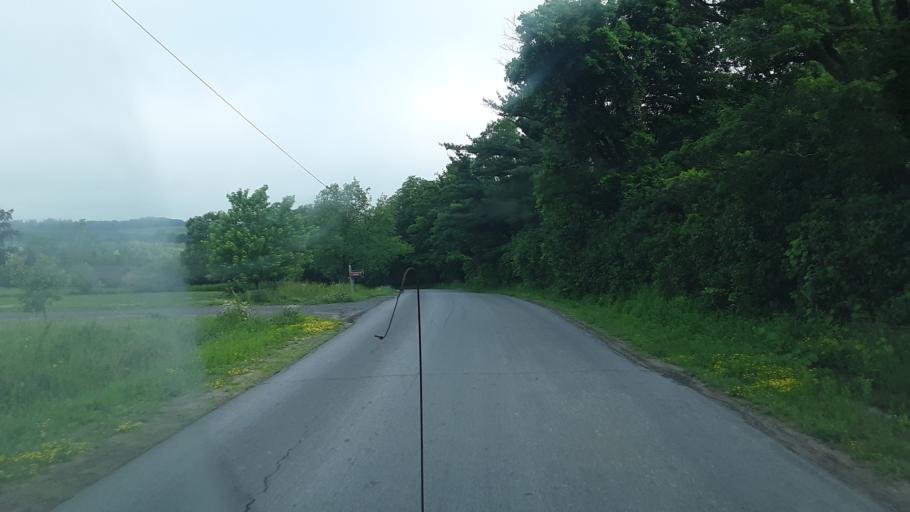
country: US
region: New York
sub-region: Montgomery County
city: Fonda
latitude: 42.8754
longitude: -74.3768
